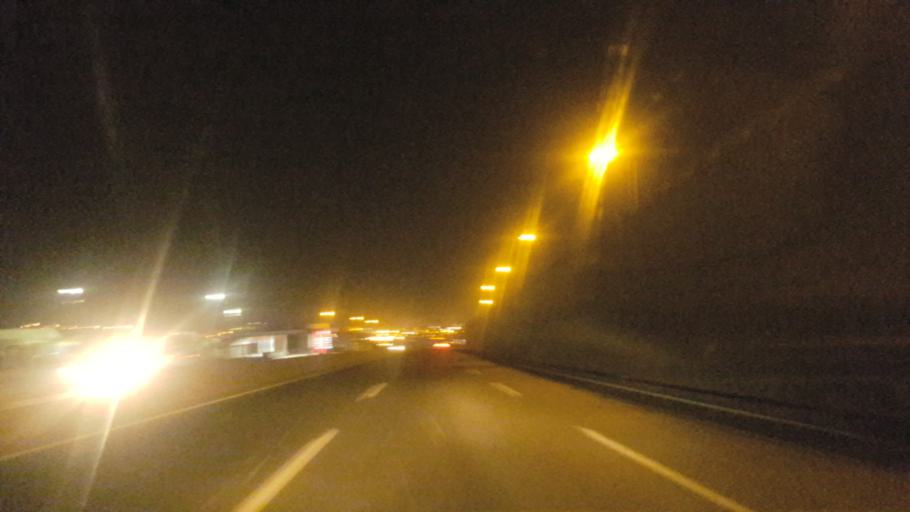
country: TR
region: Kocaeli
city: Tavsanli
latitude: 40.8053
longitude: 29.5273
